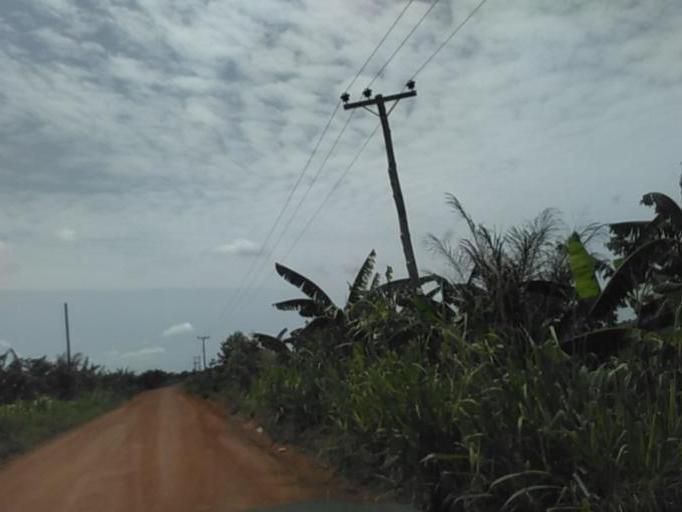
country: GH
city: Akropong
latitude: 6.0963
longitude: 0.2030
